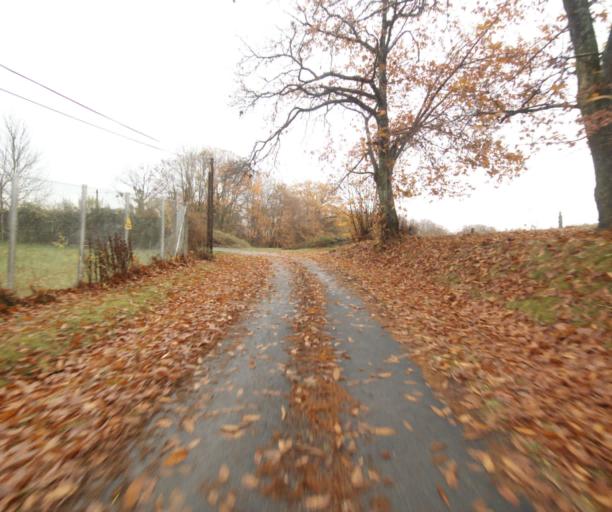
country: FR
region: Limousin
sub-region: Departement de la Correze
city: Cornil
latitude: 45.1909
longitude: 1.6395
